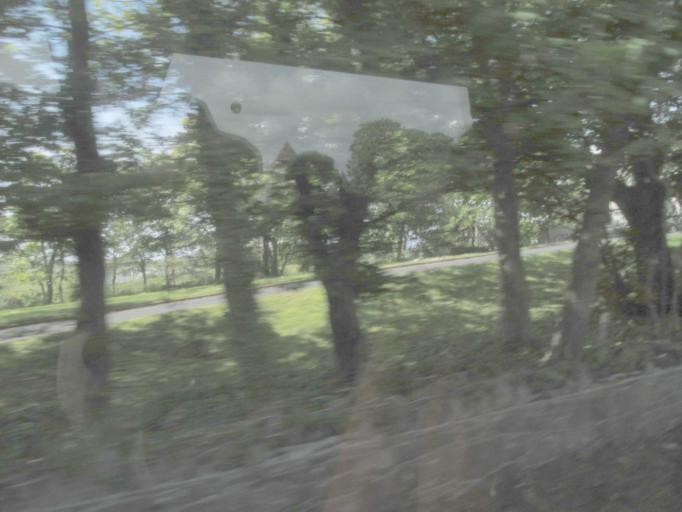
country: GB
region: Northern Ireland
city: Bushmills
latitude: 55.2001
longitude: -6.5282
